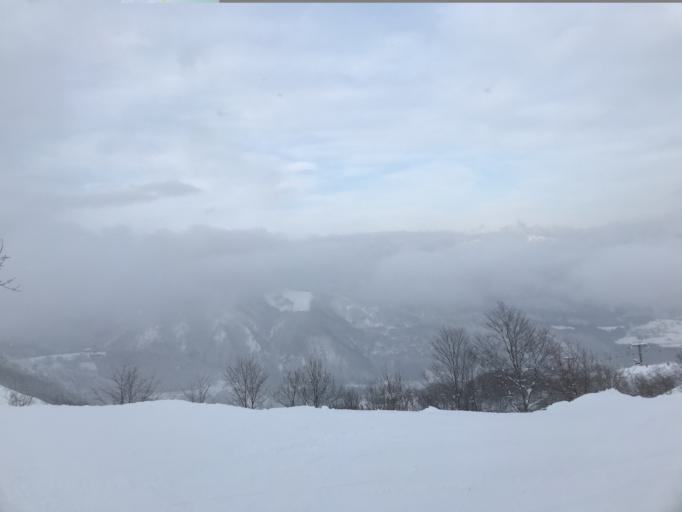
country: JP
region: Nagano
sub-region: Kitaazumi Gun
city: Hakuba
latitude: 36.6984
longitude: 137.8148
